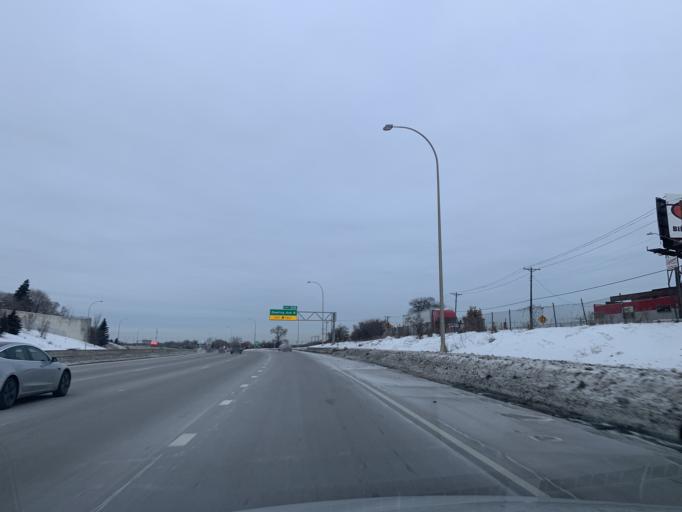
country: US
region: Minnesota
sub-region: Anoka County
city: Columbia Heights
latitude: 45.0180
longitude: -93.2822
